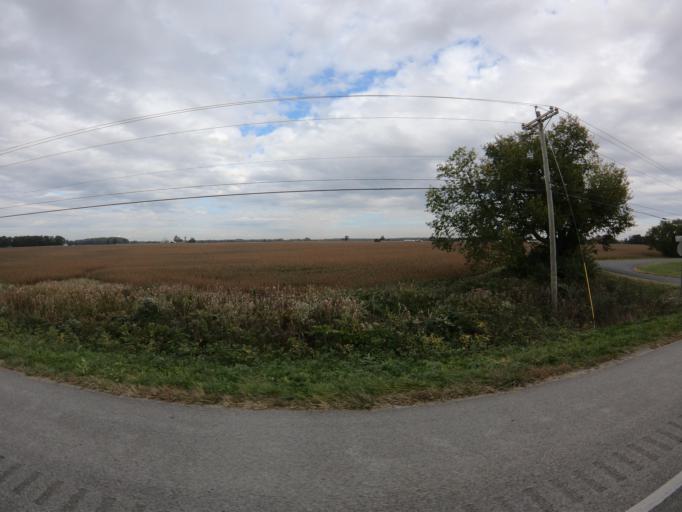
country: US
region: Maryland
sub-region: Queen Anne's County
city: Centreville
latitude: 38.9554
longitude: -76.0849
